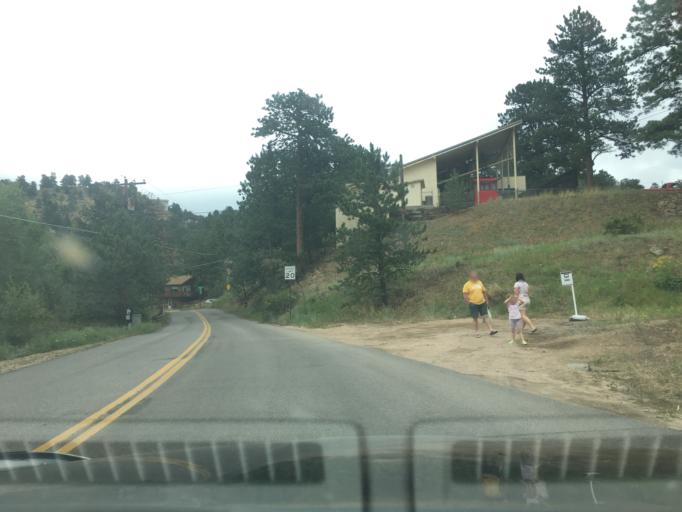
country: US
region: Colorado
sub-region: Larimer County
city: Estes Park
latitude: 40.3713
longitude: -105.5234
